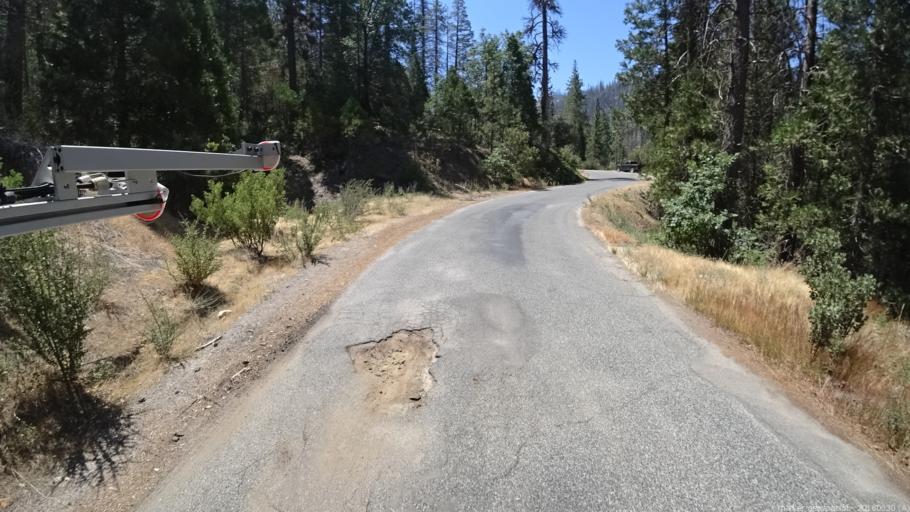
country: US
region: California
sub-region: Madera County
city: Oakhurst
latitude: 37.3629
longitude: -119.3518
